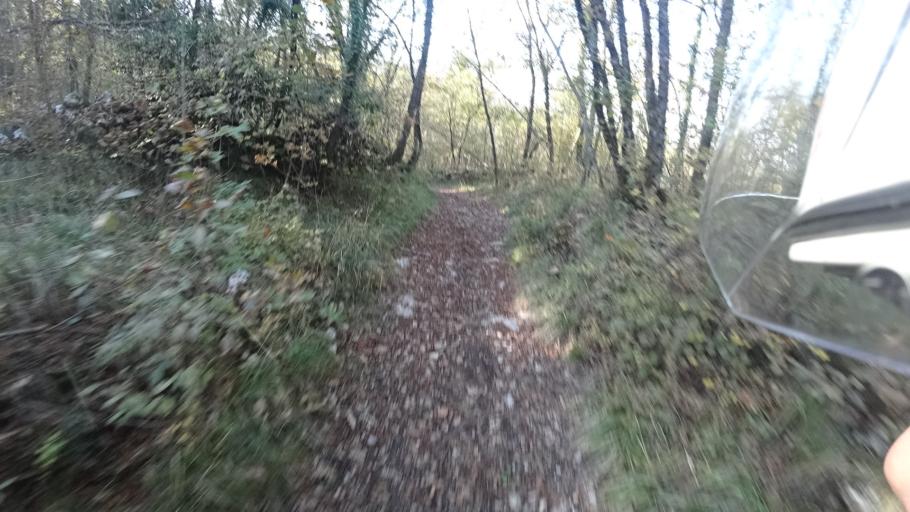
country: HR
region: Primorsko-Goranska
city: Matulji
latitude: 45.4041
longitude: 14.2885
